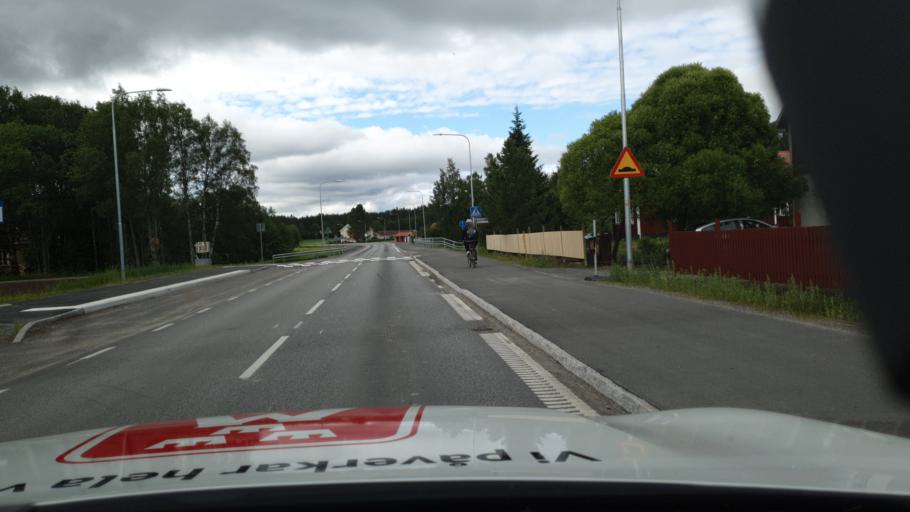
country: SE
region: Vaesterbotten
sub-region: Umea Kommun
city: Roback
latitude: 63.8069
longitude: 20.2013
